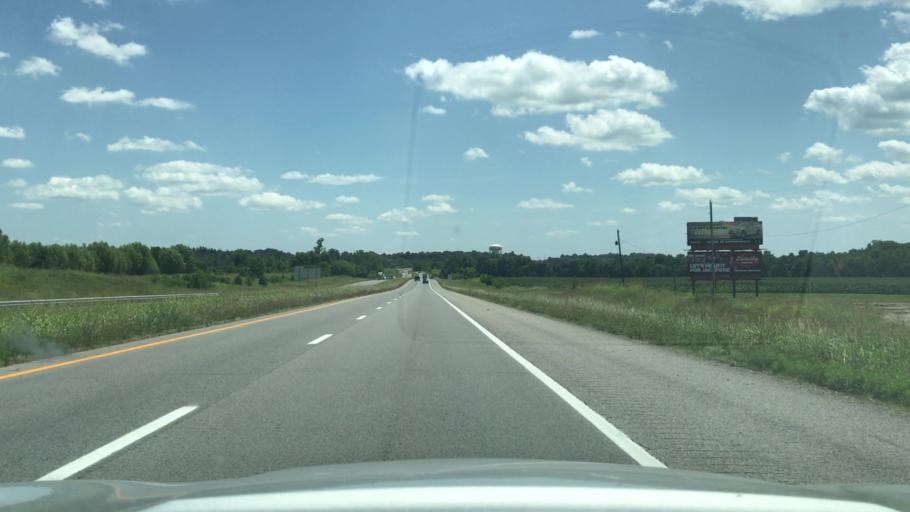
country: US
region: Kentucky
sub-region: Christian County
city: Hopkinsville
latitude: 36.8899
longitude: -87.4692
